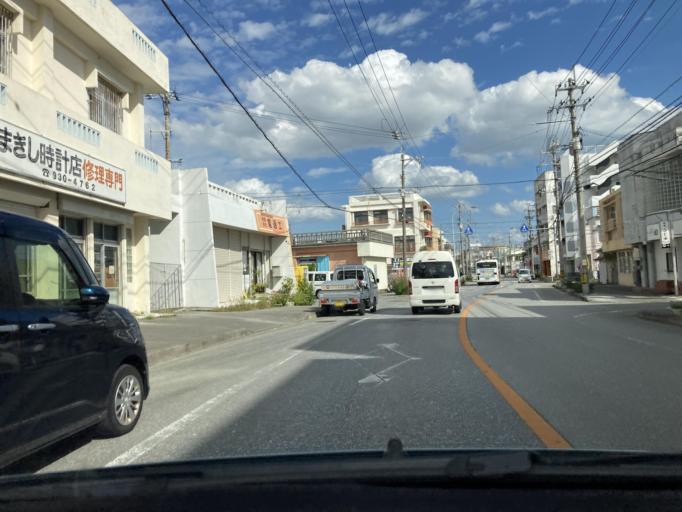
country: JP
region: Okinawa
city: Chatan
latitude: 26.3201
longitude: 127.7827
